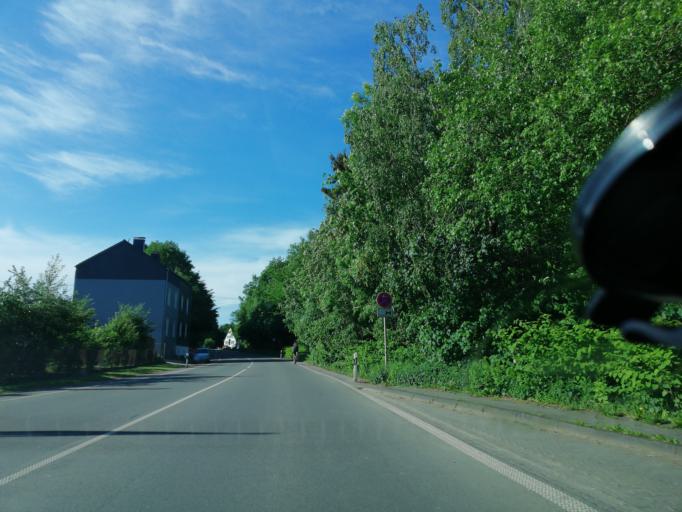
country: DE
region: North Rhine-Westphalia
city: Gevelsberg
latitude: 51.3600
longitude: 7.3292
